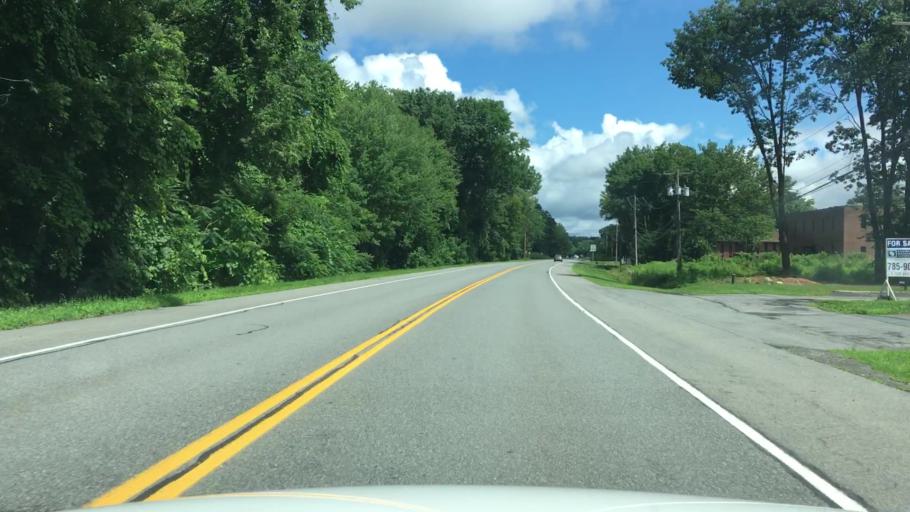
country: US
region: New York
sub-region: Albany County
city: Colonie
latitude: 42.7362
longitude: -73.8461
